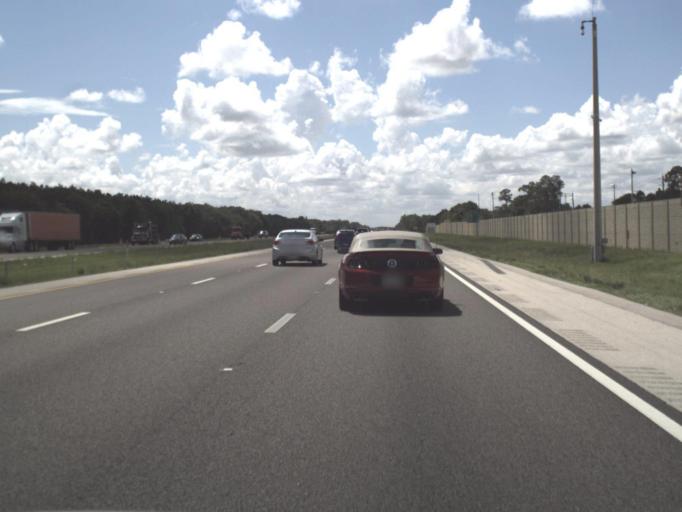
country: US
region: Florida
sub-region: Lee County
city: Three Oaks
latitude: 26.4787
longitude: -81.7928
